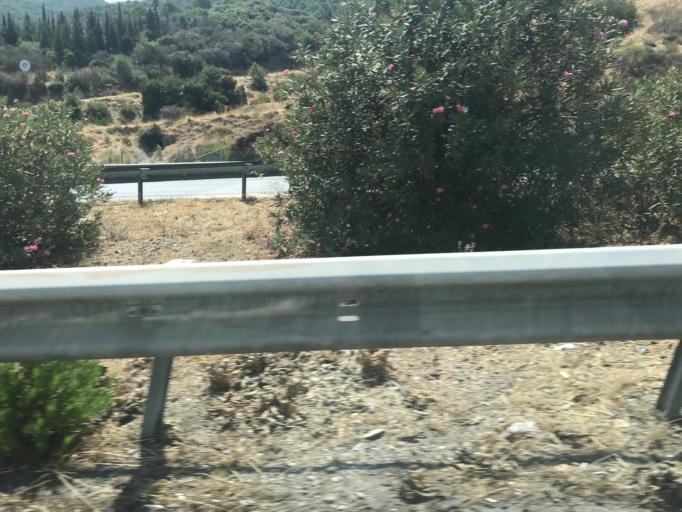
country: TR
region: Izmir
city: Urla
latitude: 38.3789
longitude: 26.9346
